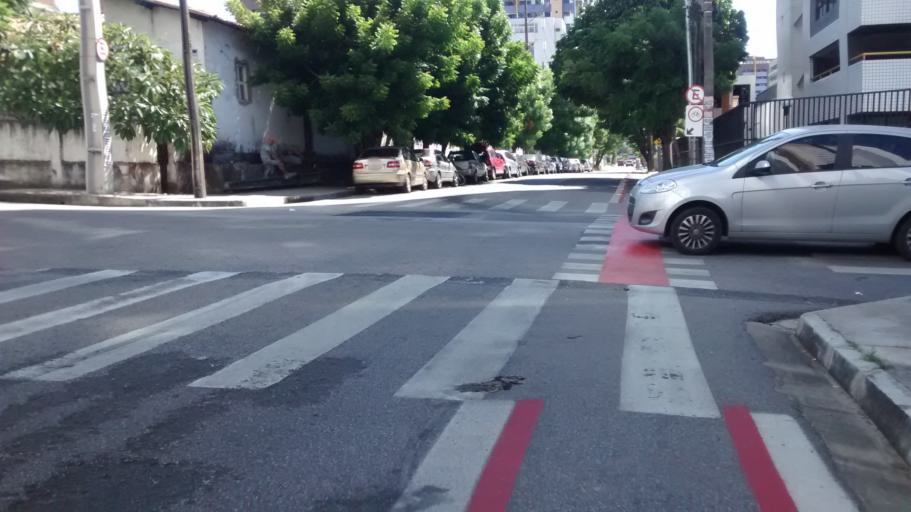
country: BR
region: Ceara
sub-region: Fortaleza
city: Fortaleza
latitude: -3.7438
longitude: -38.5050
